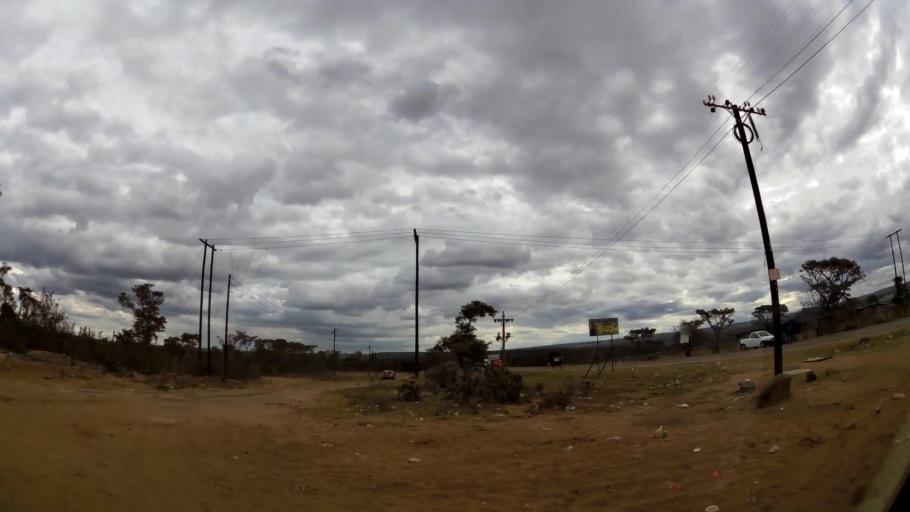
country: ZA
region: Limpopo
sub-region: Waterberg District Municipality
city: Modimolle
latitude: -24.6897
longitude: 28.4191
